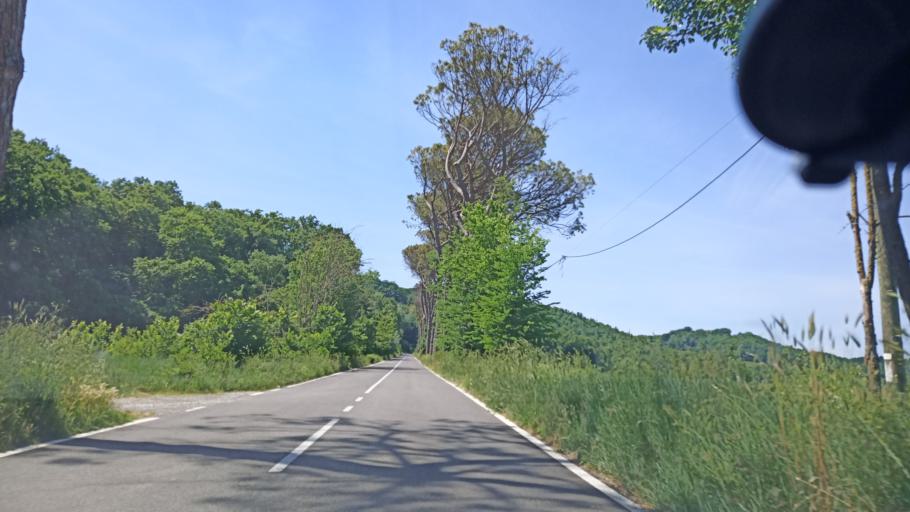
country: IT
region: Latium
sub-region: Provincia di Rieti
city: Stimigliano
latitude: 42.3105
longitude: 12.5718
